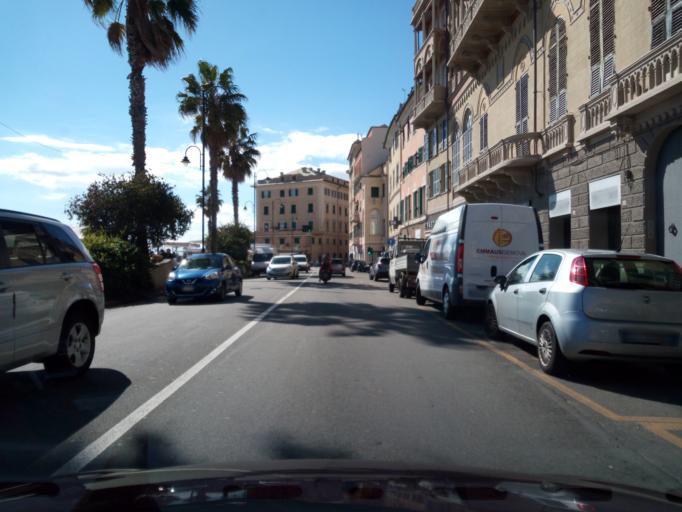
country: IT
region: Liguria
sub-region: Provincia di Genova
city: Mele
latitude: 44.4249
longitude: 8.8162
